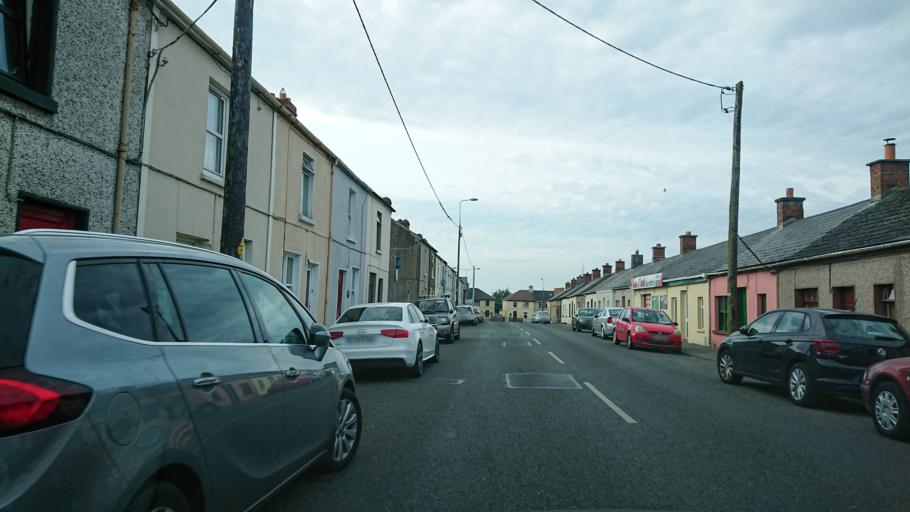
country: IE
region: Munster
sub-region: Waterford
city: Waterford
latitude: 52.2564
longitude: -7.1217
